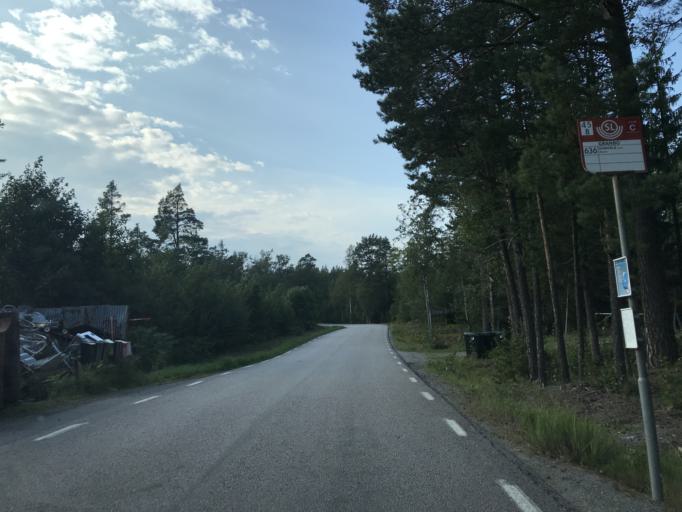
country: SE
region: Stockholm
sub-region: Norrtalje Kommun
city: Bjorko
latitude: 59.8681
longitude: 19.0250
